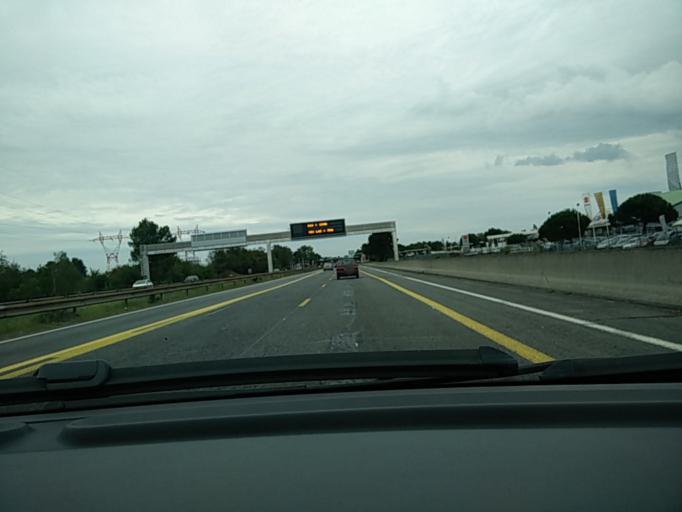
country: FR
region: Aquitaine
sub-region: Departement de la Gironde
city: Le Haillan
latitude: 44.8469
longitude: -0.6698
